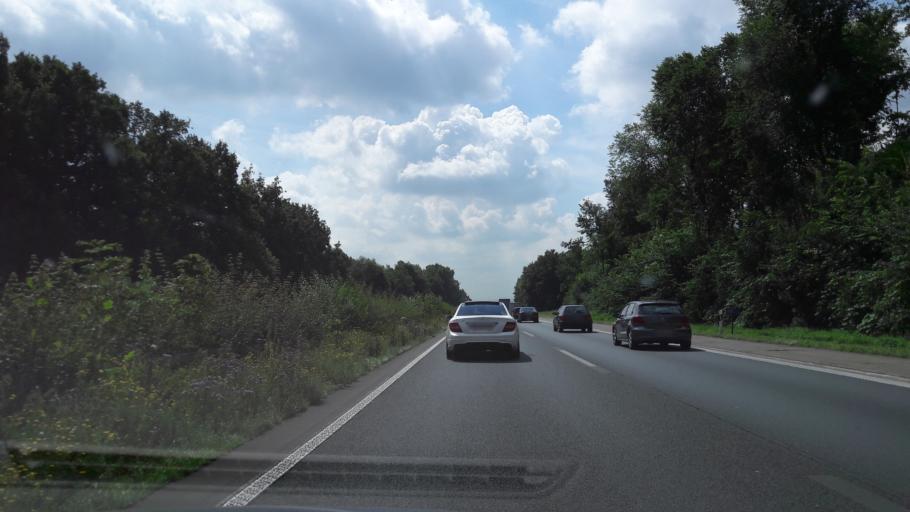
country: DE
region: North Rhine-Westphalia
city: Werne
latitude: 51.6746
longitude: 7.6800
